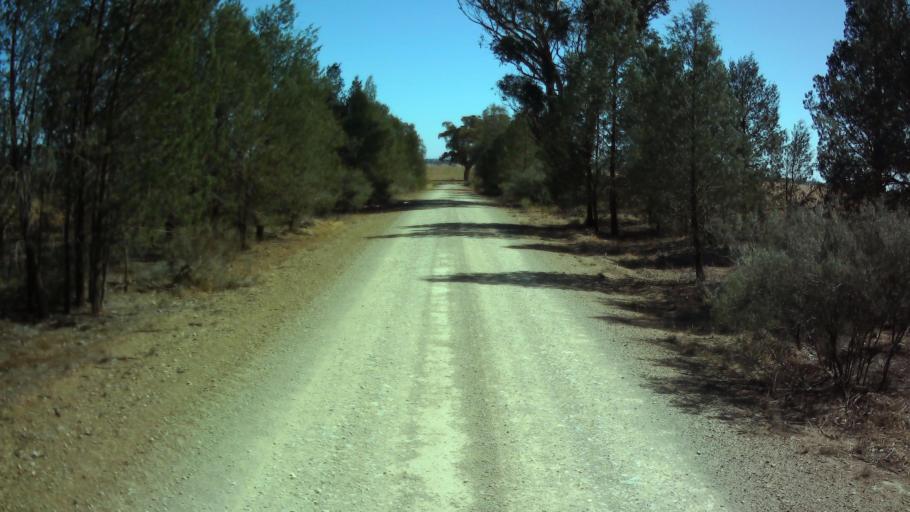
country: AU
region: New South Wales
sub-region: Weddin
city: Grenfell
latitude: -33.8756
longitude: 147.8742
